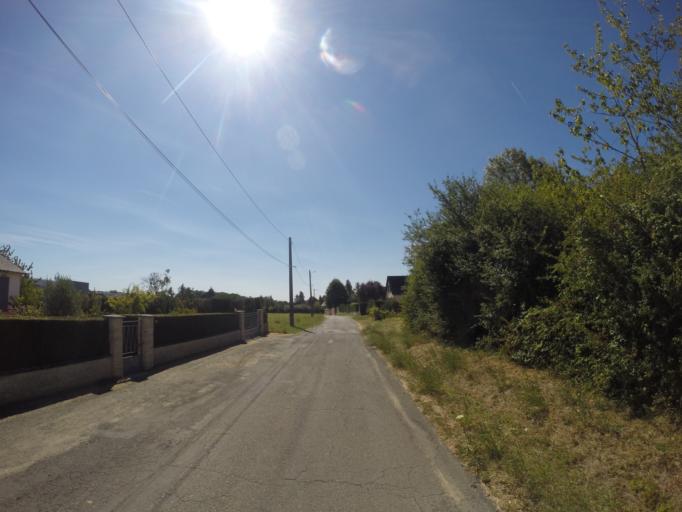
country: FR
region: Centre
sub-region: Departement d'Indre-et-Loire
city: Parcay-Meslay
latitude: 47.4207
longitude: 0.7129
